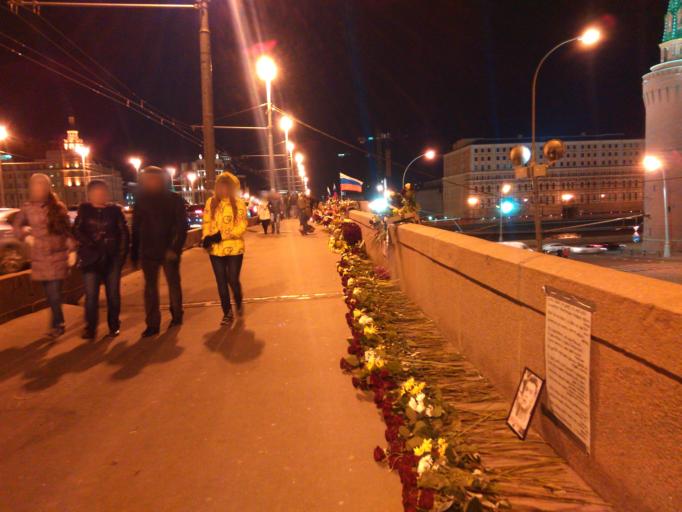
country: RU
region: Moscow
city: Moscow
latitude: 55.7505
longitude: 37.6241
